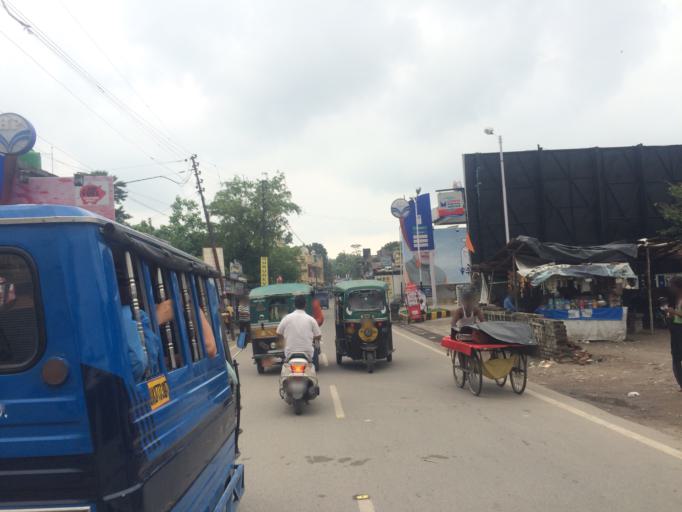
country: IN
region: Uttarakhand
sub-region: Dehradun
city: Rishikesh
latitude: 30.1120
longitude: 78.3029
